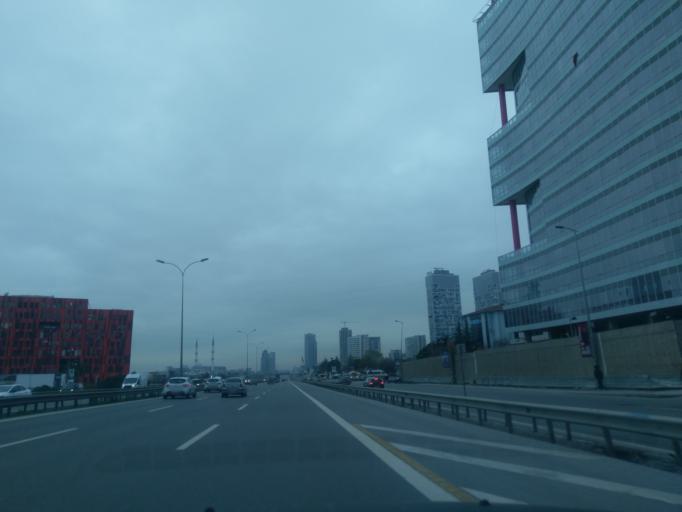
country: TR
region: Istanbul
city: Maltepe
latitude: 40.9114
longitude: 29.1961
